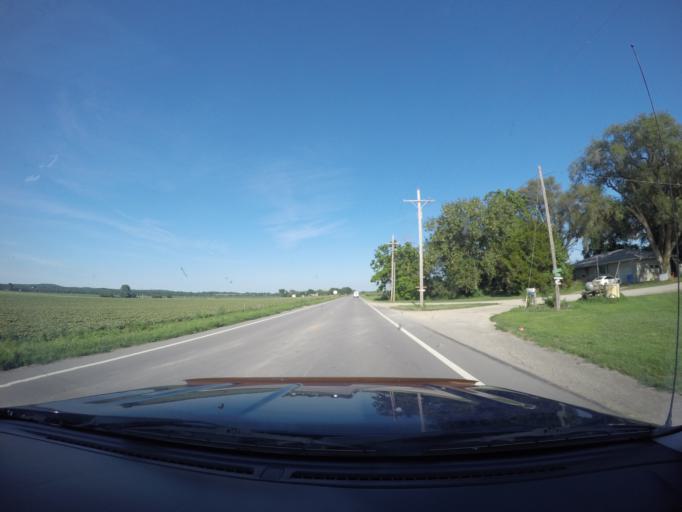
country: US
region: Kansas
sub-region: Douglas County
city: Lawrence
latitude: 39.0007
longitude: -95.2120
